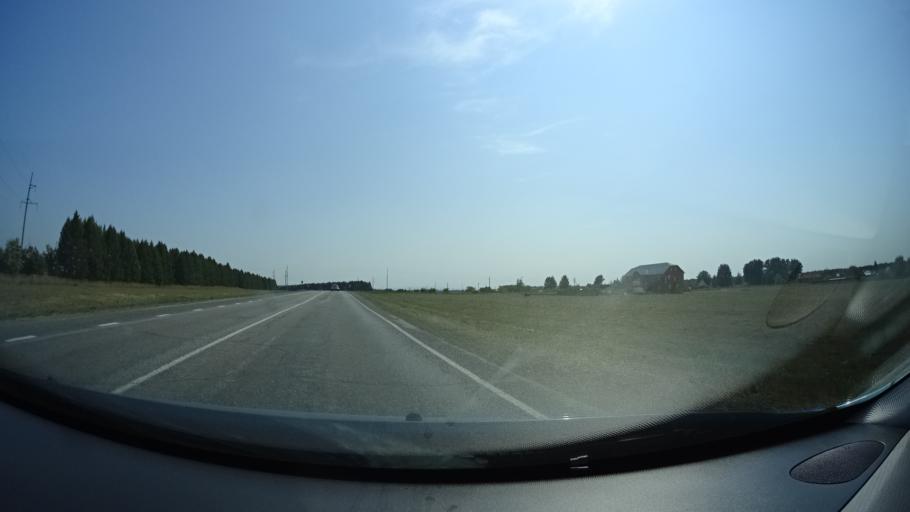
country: RU
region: Bashkortostan
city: Ulukulevo
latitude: 54.4531
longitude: 56.5233
